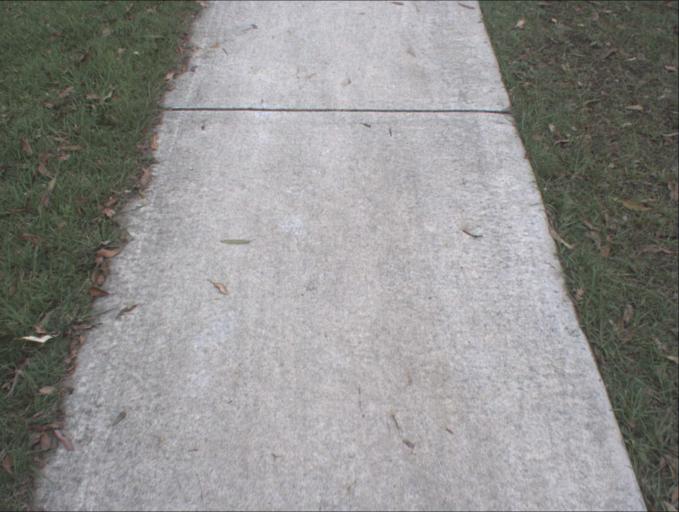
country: AU
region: Queensland
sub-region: Logan
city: North Maclean
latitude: -27.7453
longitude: 153.0177
